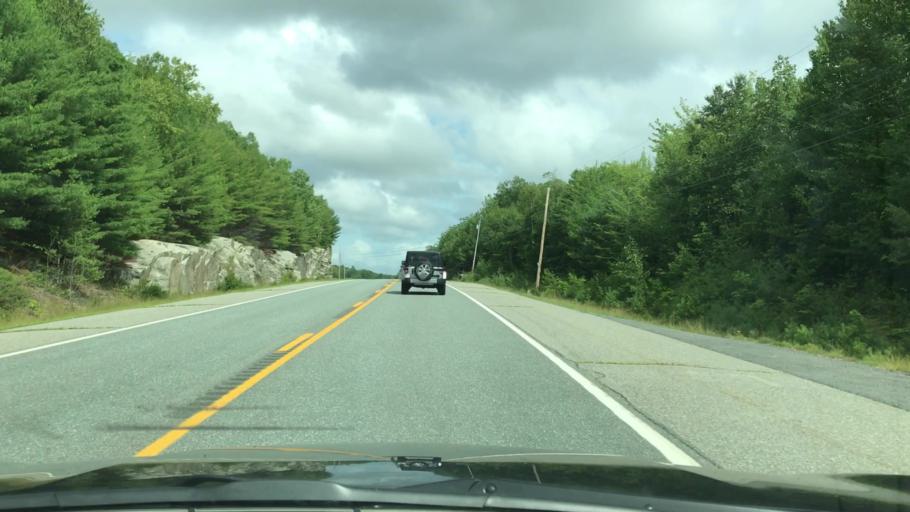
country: US
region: Maine
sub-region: Hancock County
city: Surry
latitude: 44.5645
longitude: -68.6020
